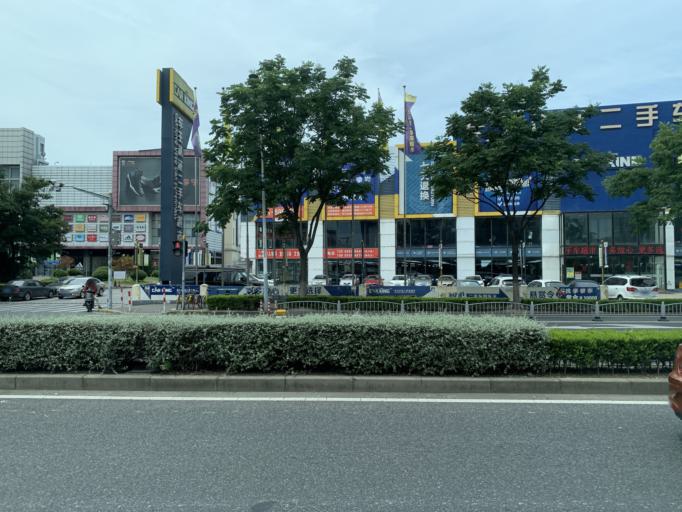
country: CN
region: Shanghai Shi
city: Kangqiao
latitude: 31.1571
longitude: 121.5604
